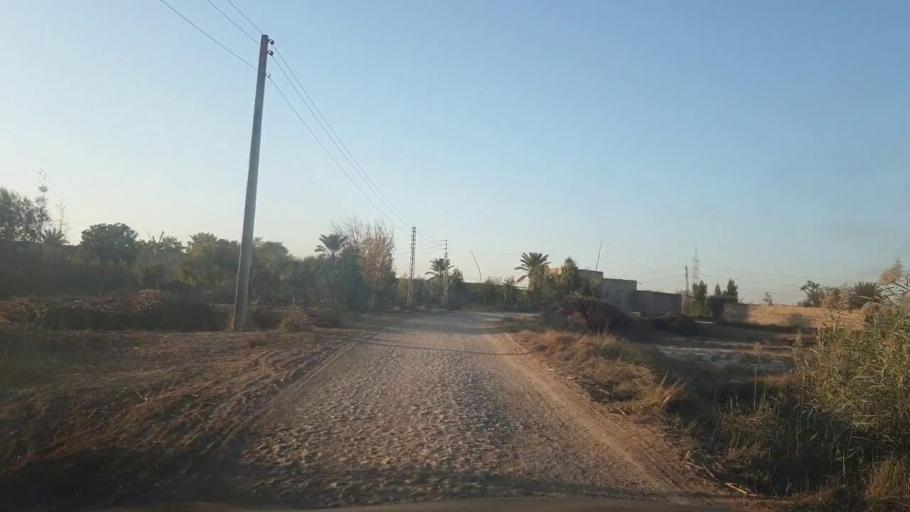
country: PK
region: Sindh
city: Mirpur Mathelo
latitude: 27.9854
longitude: 69.4557
